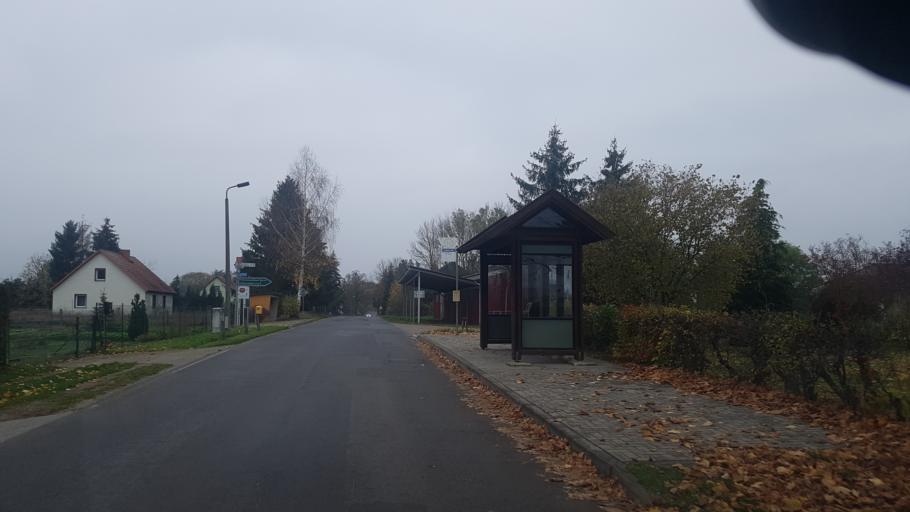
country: DE
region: Brandenburg
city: Schonermark
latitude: 52.9170
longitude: 13.1277
